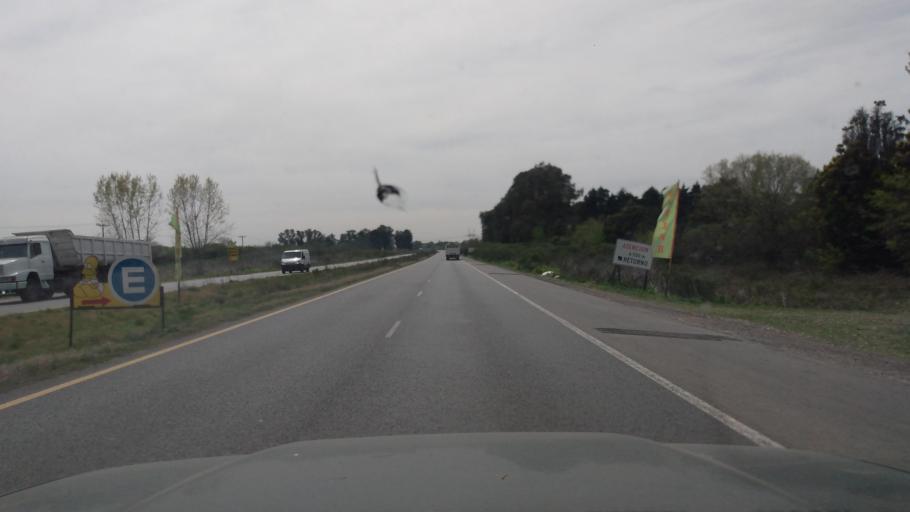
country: AR
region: Buenos Aires
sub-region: Partido de Lujan
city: Lujan
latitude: -34.4594
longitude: -59.0600
